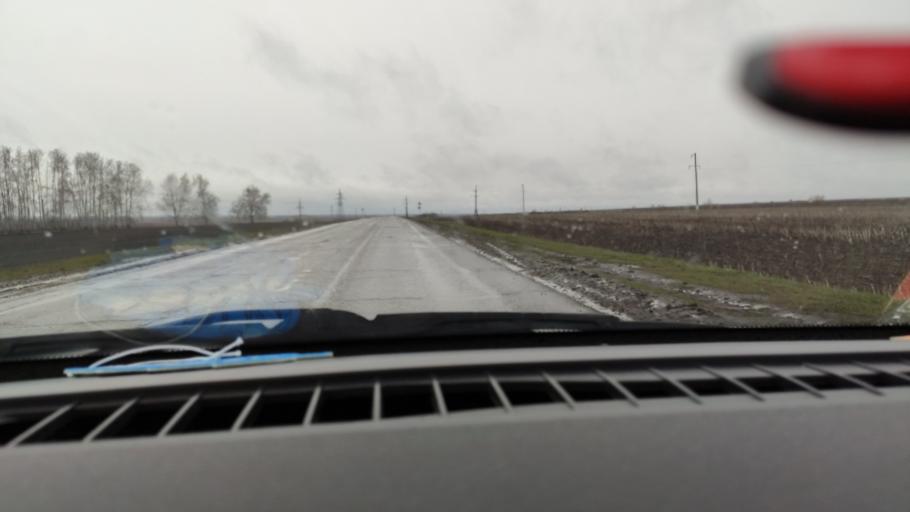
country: RU
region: Tatarstan
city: Nurlat
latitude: 54.5973
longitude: 50.8799
